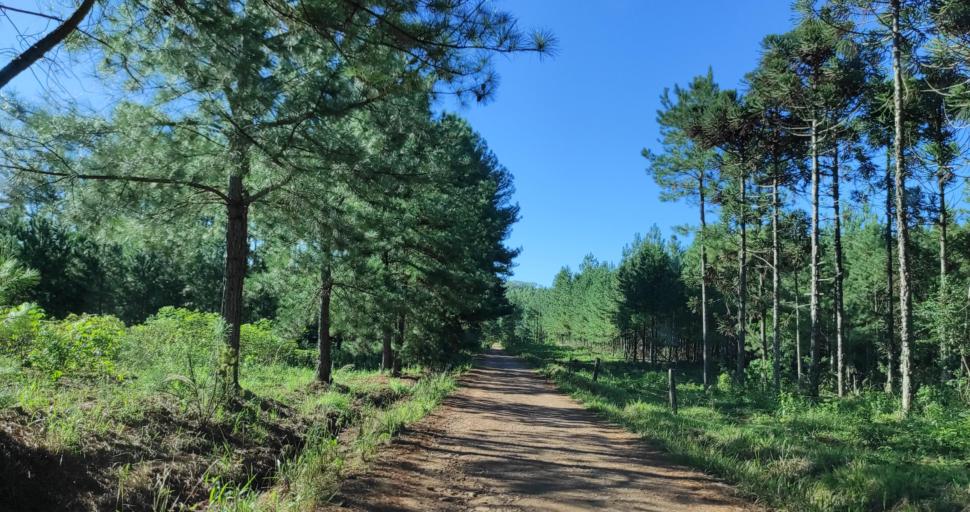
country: AR
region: Misiones
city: Capiovi
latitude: -26.9158
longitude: -54.9998
